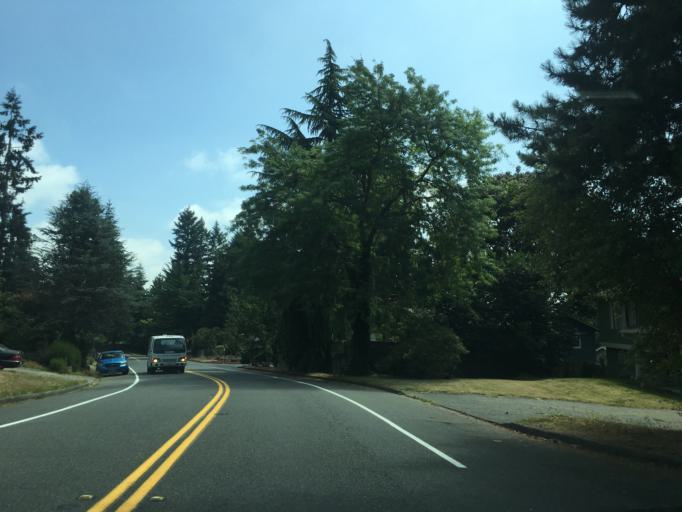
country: US
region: Washington
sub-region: King County
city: Inglewood-Finn Hill
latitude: 47.7203
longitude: -122.2193
